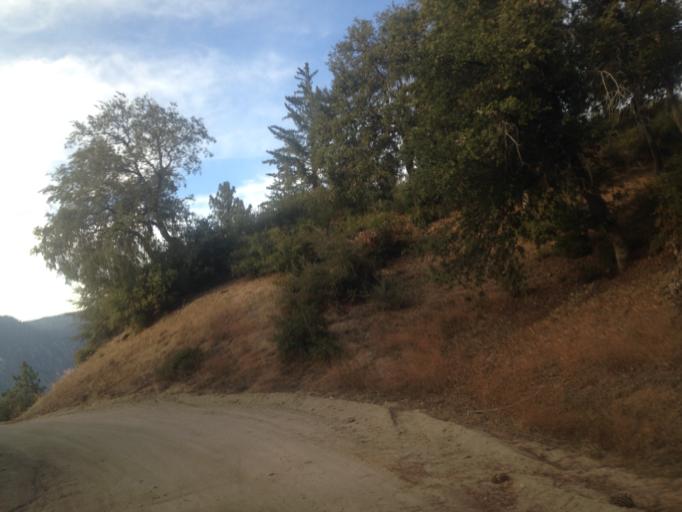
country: US
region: California
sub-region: San Bernardino County
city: Yucaipa
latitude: 34.1455
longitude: -116.9926
